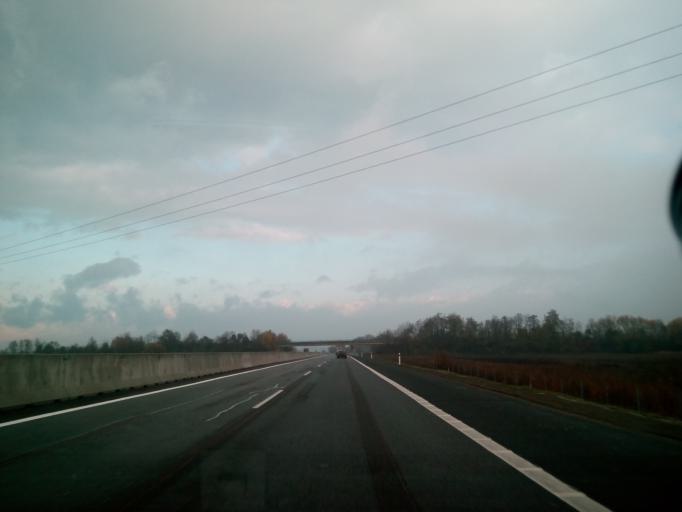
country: SK
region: Kosicky
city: Kosice
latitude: 48.8125
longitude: 21.3098
